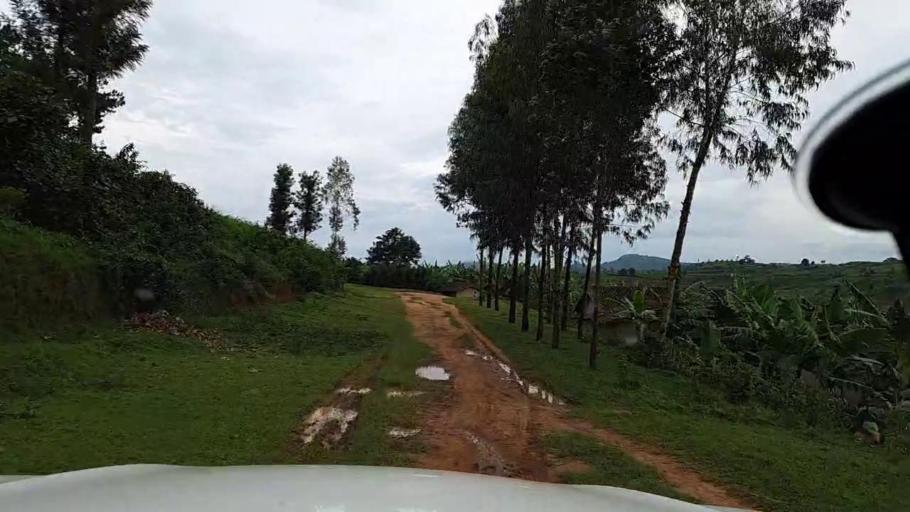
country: RW
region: Southern Province
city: Gitarama
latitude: -2.1170
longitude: 29.6461
